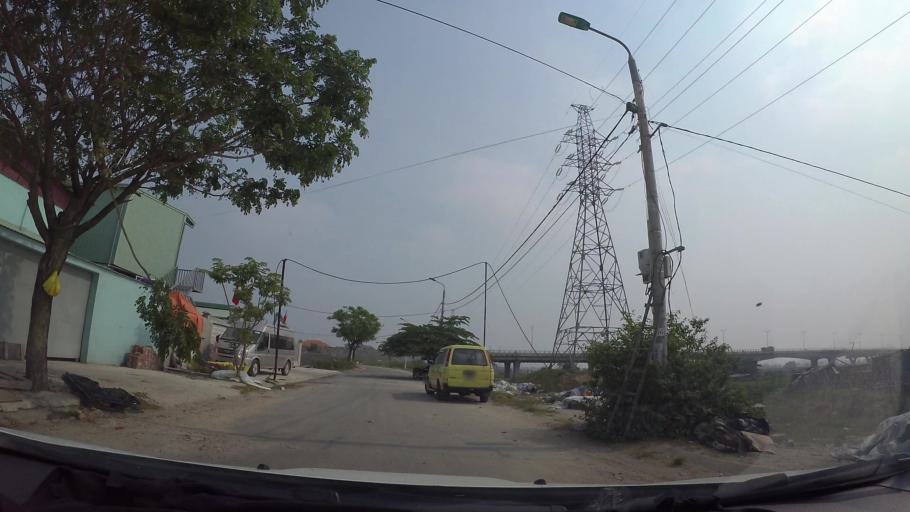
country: VN
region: Da Nang
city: Cam Le
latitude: 16.0010
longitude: 108.2268
